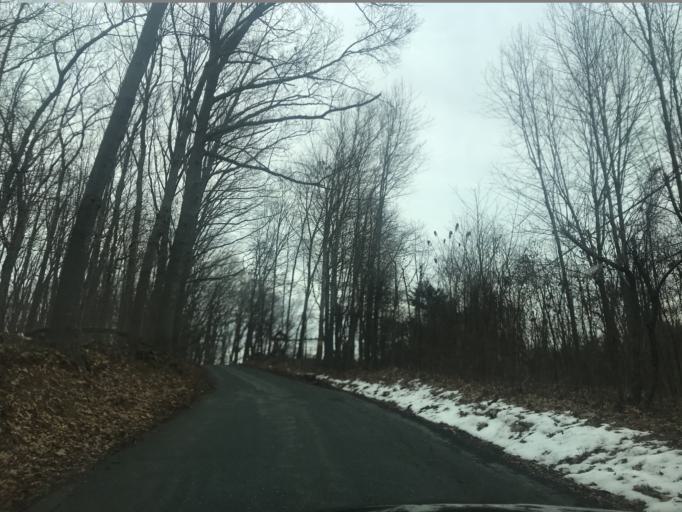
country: US
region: Pennsylvania
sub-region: York County
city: Stewartstown
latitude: 39.6940
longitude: -76.5221
